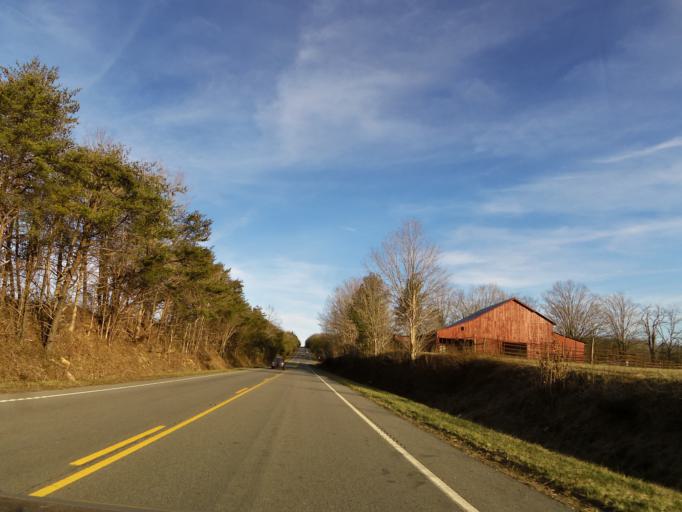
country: US
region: Tennessee
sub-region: Cumberland County
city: Crossville
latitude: 35.9653
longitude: -85.1429
